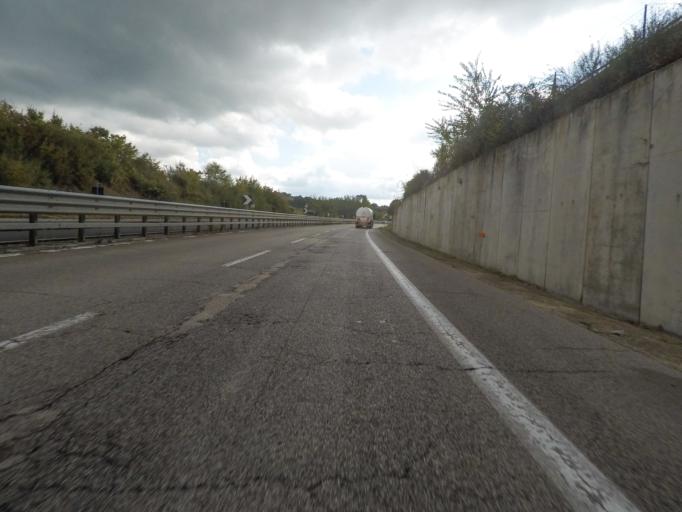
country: IT
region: Tuscany
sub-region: Provincia di Siena
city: Rapolano Terme
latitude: 43.3097
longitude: 11.5847
